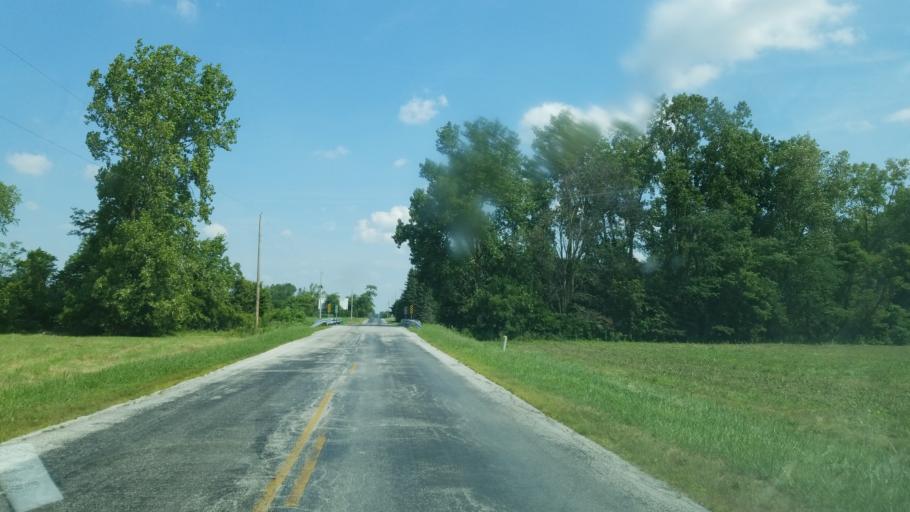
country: US
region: Ohio
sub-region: Seneca County
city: Fostoria
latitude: 41.2396
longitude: -83.5352
